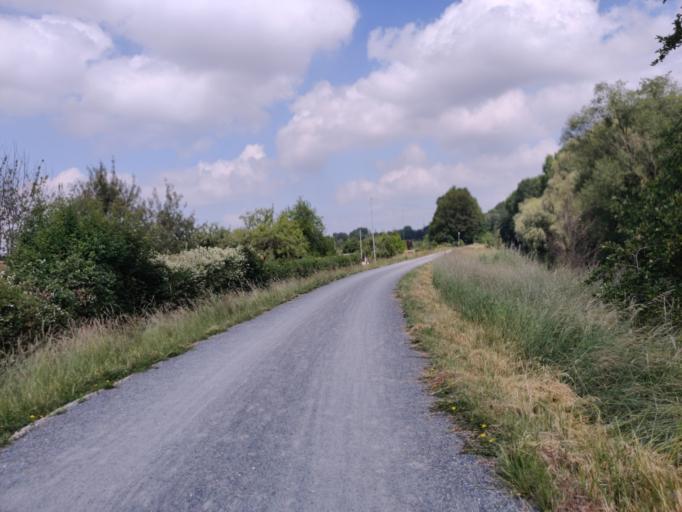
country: DE
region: Lower Saxony
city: Hildesheim
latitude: 52.1329
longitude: 9.9576
